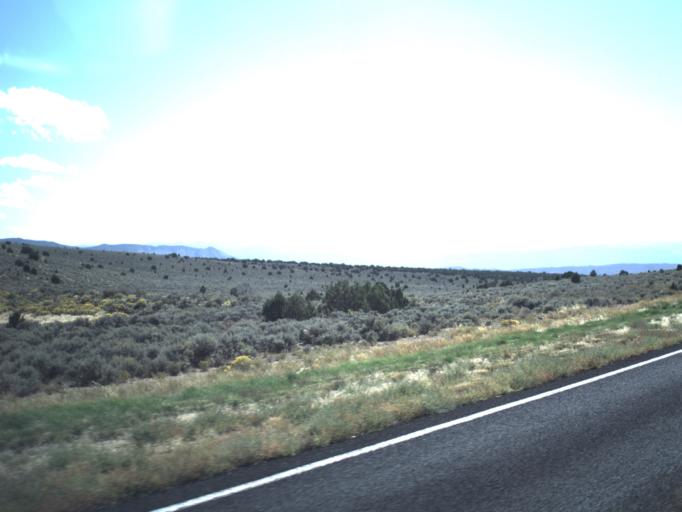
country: US
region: Utah
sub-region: Iron County
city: Parowan
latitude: 38.0310
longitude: -112.9983
